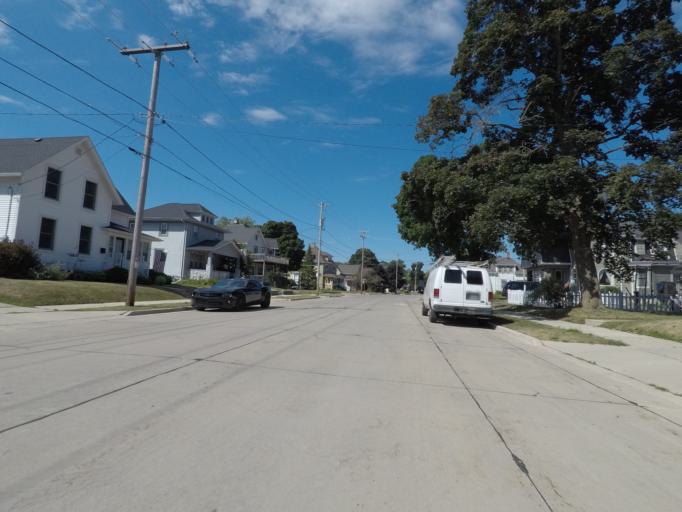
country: US
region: Wisconsin
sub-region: Waukesha County
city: Waukesha
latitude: 43.0090
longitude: -88.2143
